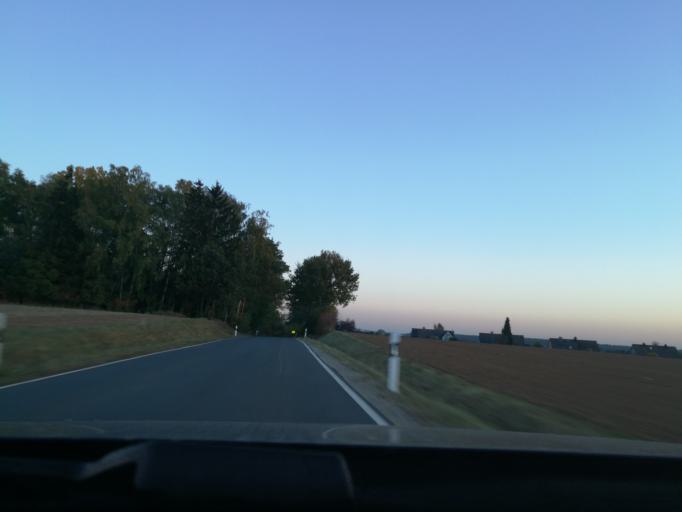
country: DE
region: Bavaria
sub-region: Regierungsbezirk Mittelfranken
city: Obermichelbach
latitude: 49.5532
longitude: 10.9150
